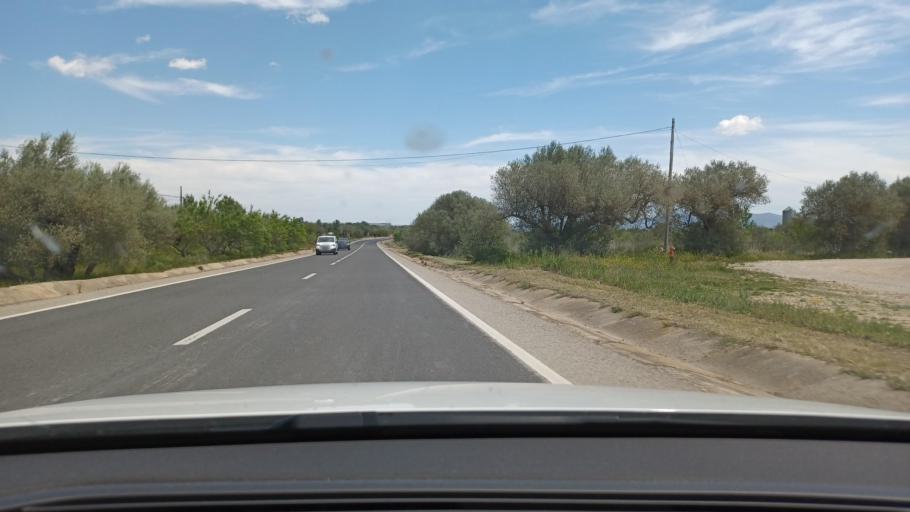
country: ES
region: Valencia
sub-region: Provincia de Castello
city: Rosell
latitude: 40.6316
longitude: 0.3029
